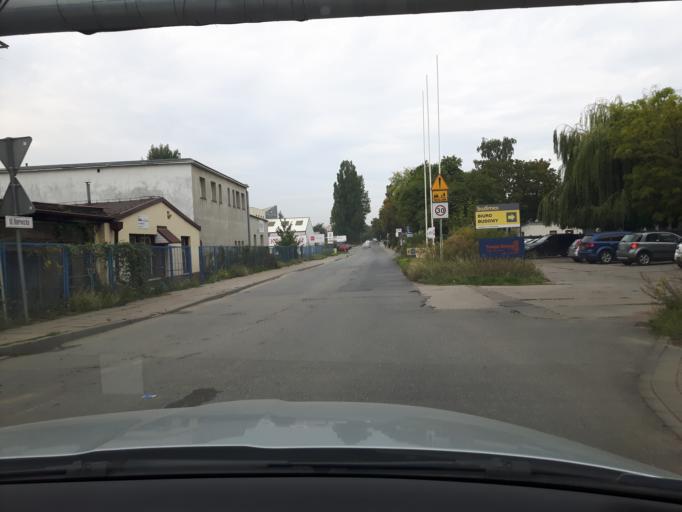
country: PL
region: Pomeranian Voivodeship
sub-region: Gdansk
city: Gdansk
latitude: 54.3823
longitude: 18.6377
